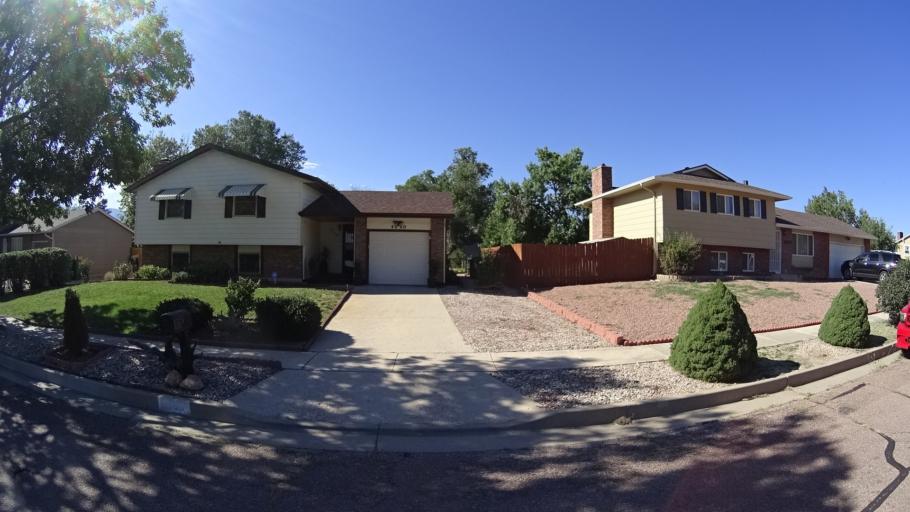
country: US
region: Colorado
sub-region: El Paso County
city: Stratmoor
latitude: 38.7933
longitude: -104.7521
